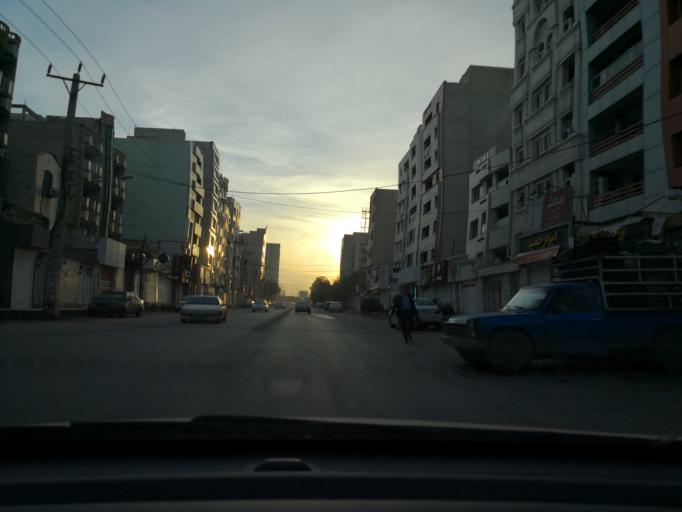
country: IR
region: Khuzestan
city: Ahvaz
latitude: 31.3492
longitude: 48.6909
